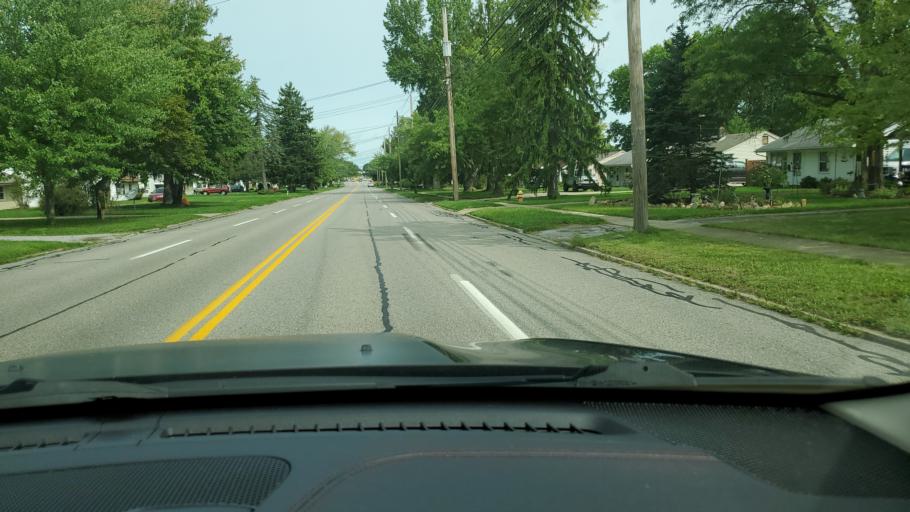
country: US
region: Ohio
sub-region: Mahoning County
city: Boardman
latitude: 41.0196
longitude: -80.6723
